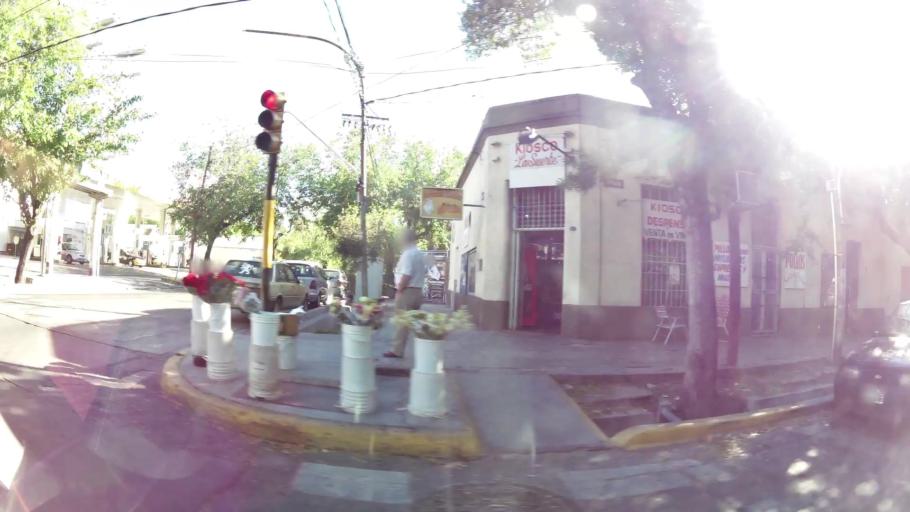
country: AR
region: Mendoza
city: Mendoza
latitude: -32.8771
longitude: -68.8564
